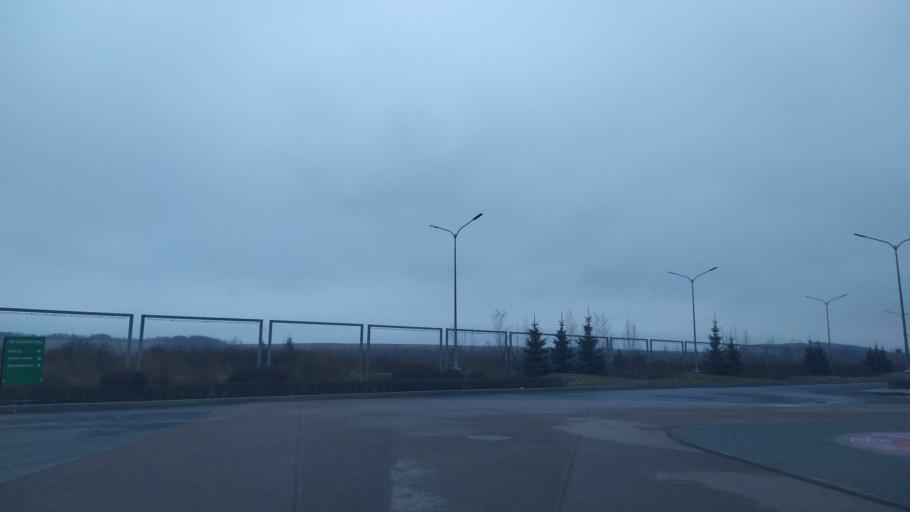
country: RU
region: St.-Petersburg
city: Aleksandrovskaya
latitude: 59.7877
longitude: 30.3184
